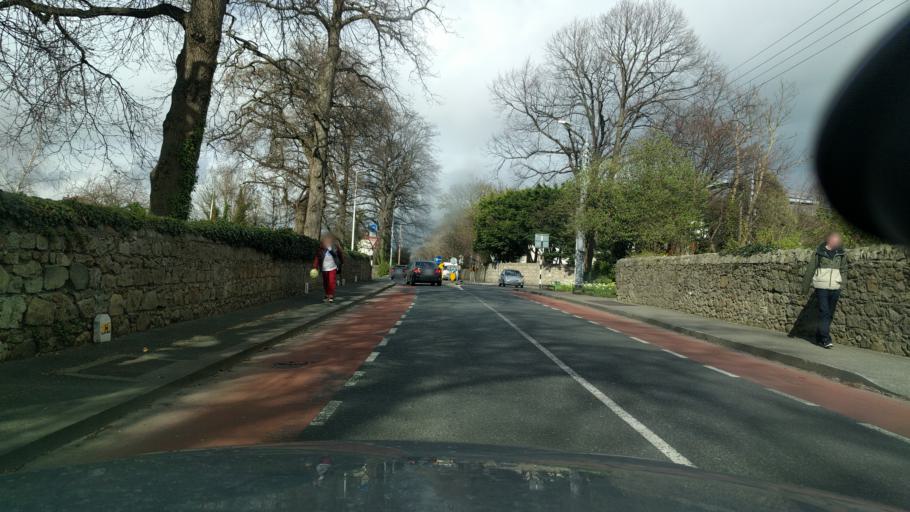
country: IE
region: Leinster
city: Shankill
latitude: 53.2282
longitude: -6.1244
